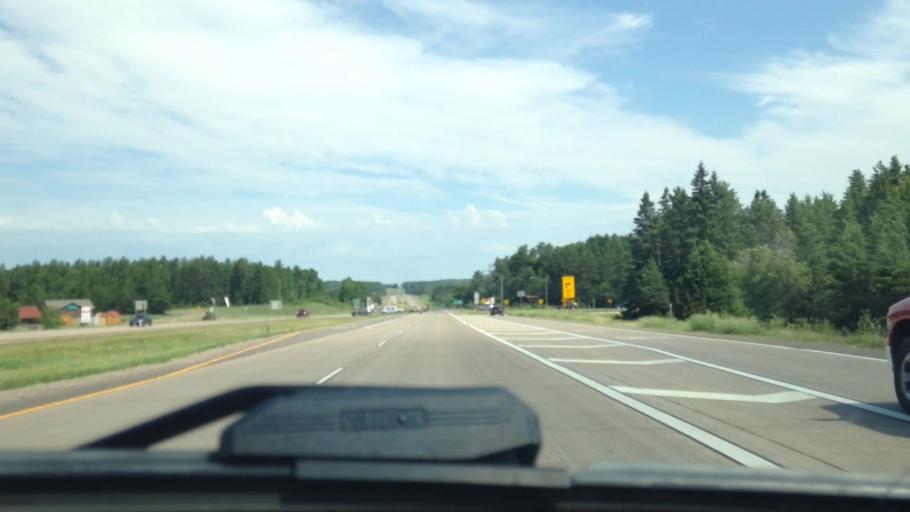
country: US
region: Wisconsin
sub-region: Washburn County
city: Spooner
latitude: 45.9037
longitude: -91.8273
